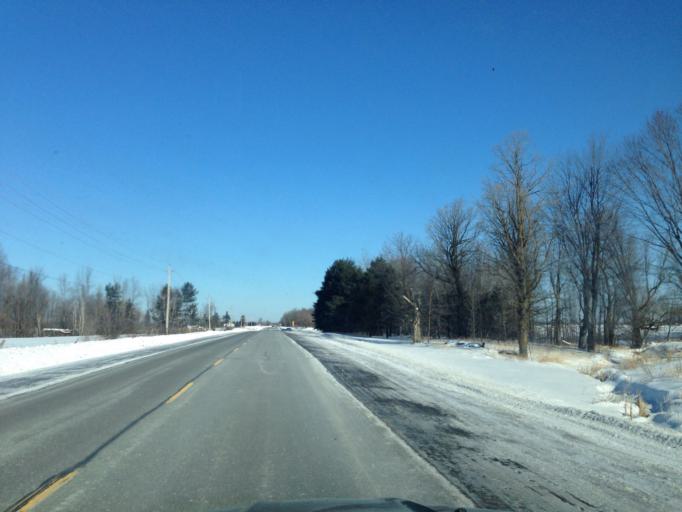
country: CA
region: Ontario
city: Clarence-Rockland
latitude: 45.2956
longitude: -75.4177
